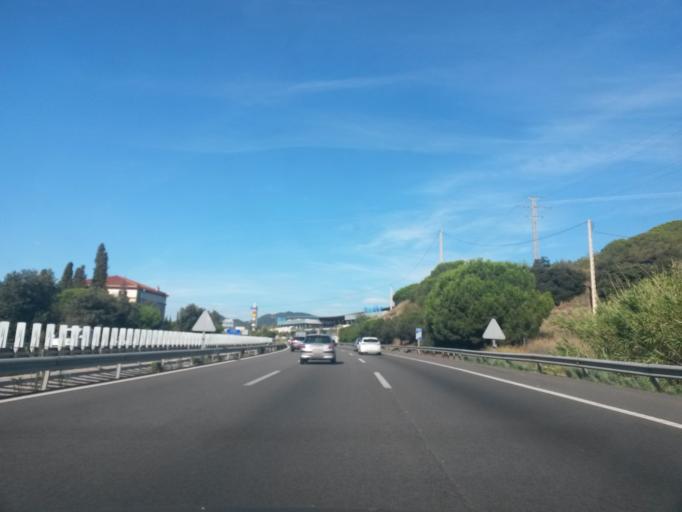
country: ES
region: Catalonia
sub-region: Provincia de Barcelona
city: Mataro
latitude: 41.5555
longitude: 2.4397
